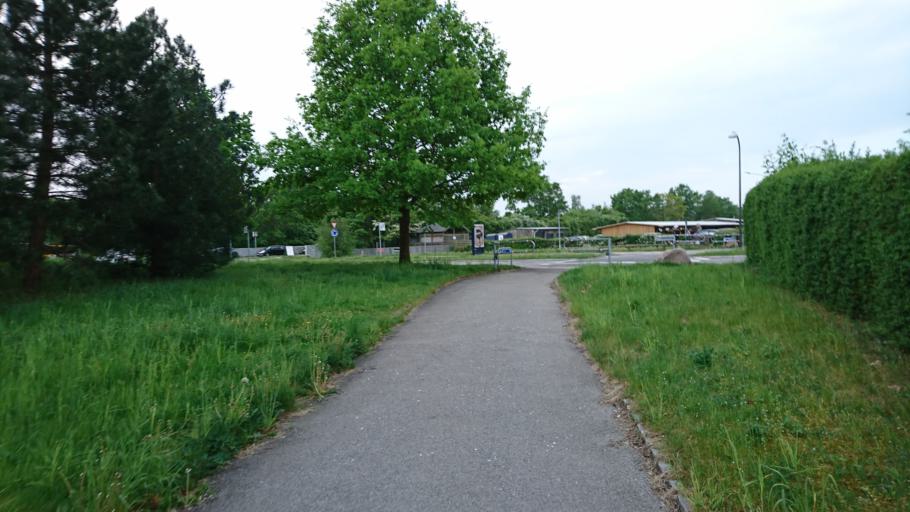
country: DK
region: Capital Region
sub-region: Ballerup Kommune
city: Ballerup
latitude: 55.7500
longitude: 12.3985
